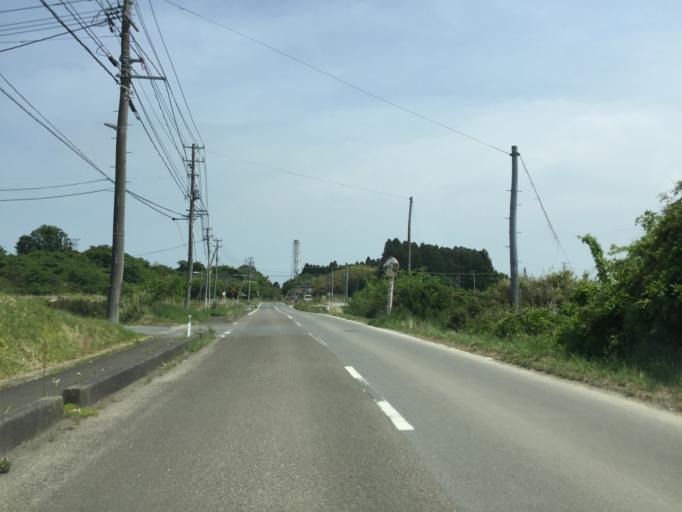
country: JP
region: Miyagi
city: Marumori
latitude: 37.8467
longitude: 140.9236
